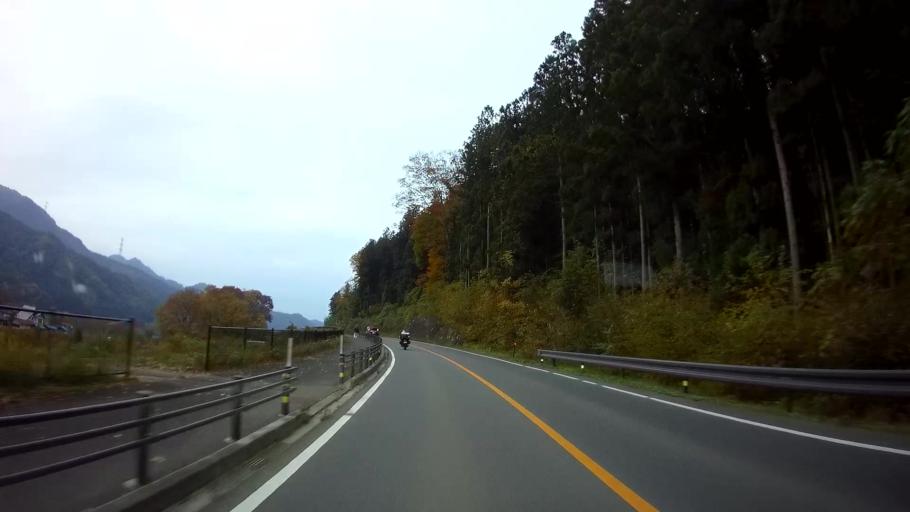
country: JP
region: Gunma
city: Nakanojomachi
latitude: 36.5667
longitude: 138.7368
